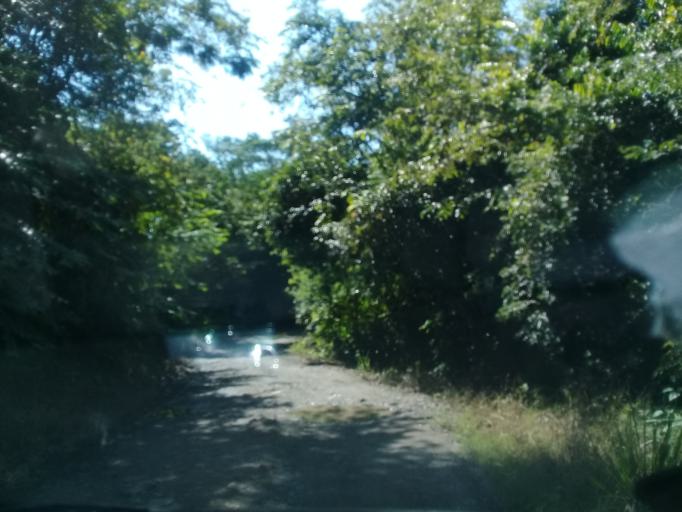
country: CO
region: Antioquia
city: Puerto Triunfo
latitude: 5.7569
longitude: -74.5680
